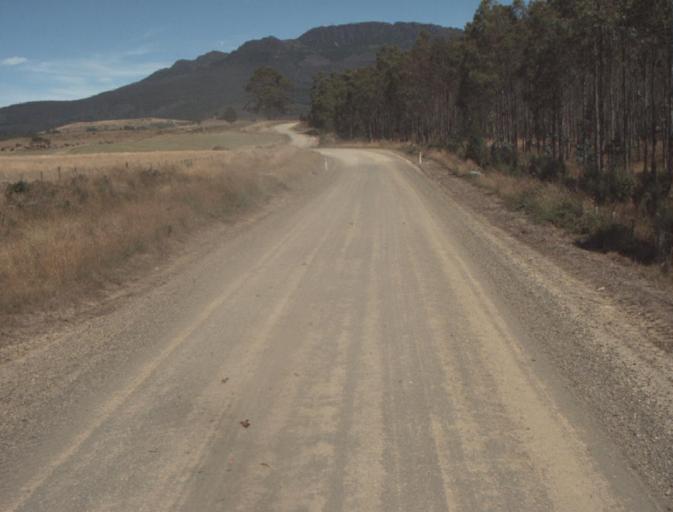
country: AU
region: Tasmania
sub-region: Dorset
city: Scottsdale
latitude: -41.3241
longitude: 147.4453
